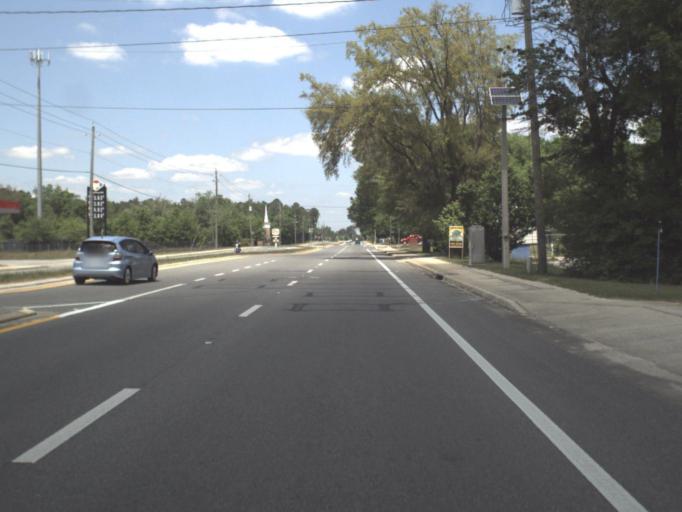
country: US
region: Florida
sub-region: Santa Rosa County
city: Point Baker
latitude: 30.6836
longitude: -87.0538
